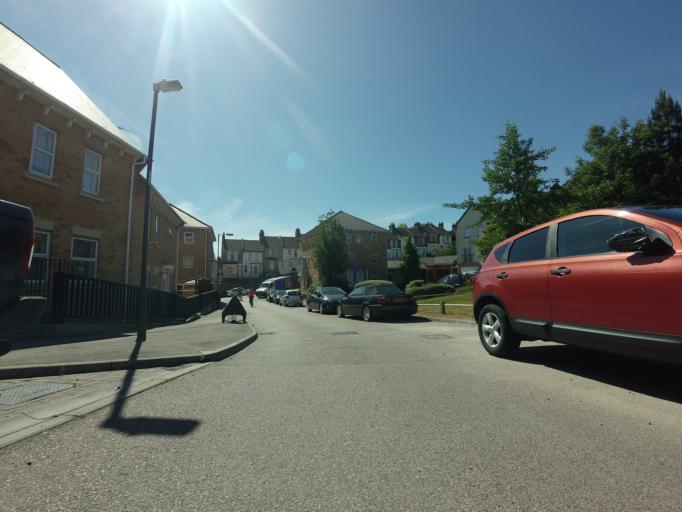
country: GB
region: England
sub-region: Kent
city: Chatham
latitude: 51.3741
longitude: 0.5331
